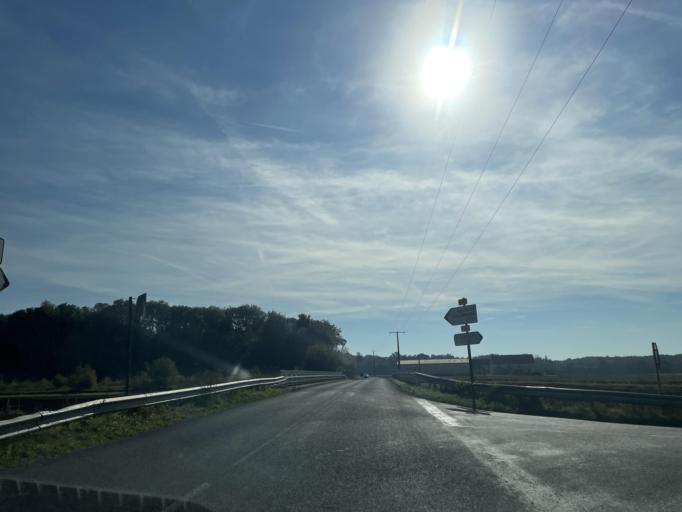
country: FR
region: Ile-de-France
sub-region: Departement de Seine-et-Marne
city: Saint-Jean-les-Deux-Jumeaux
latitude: 48.9237
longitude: 3.0042
